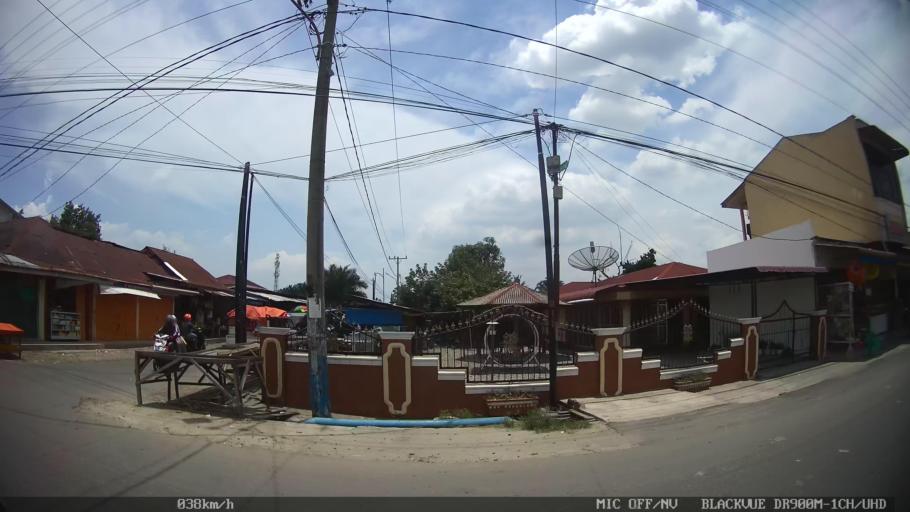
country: ID
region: North Sumatra
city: Binjai
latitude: 3.6125
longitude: 98.5181
